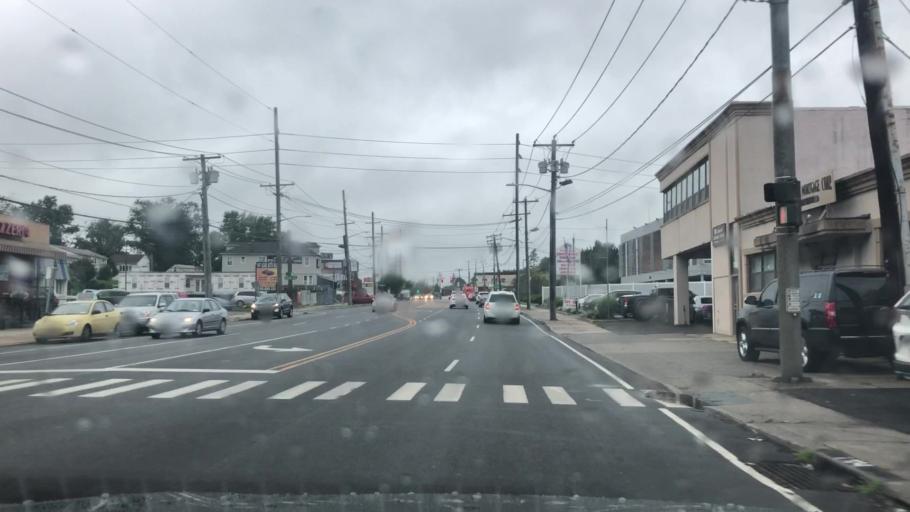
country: US
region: New York
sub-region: Nassau County
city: Franklin Square
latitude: 40.7084
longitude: -73.6842
